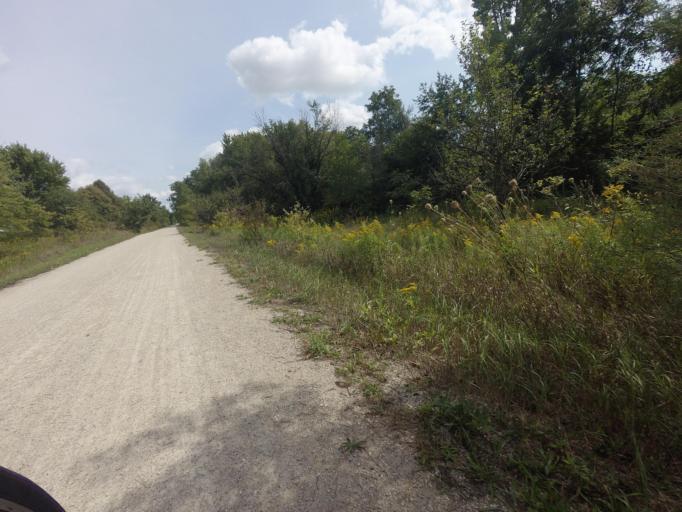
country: CA
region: Ontario
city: Waterloo
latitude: 43.6126
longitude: -80.5725
